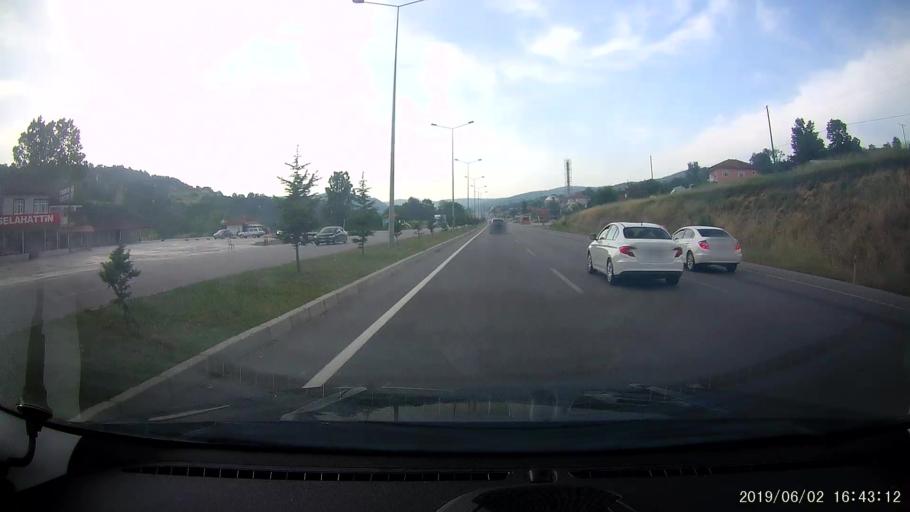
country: TR
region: Samsun
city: Kavak
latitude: 41.1314
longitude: 36.1319
